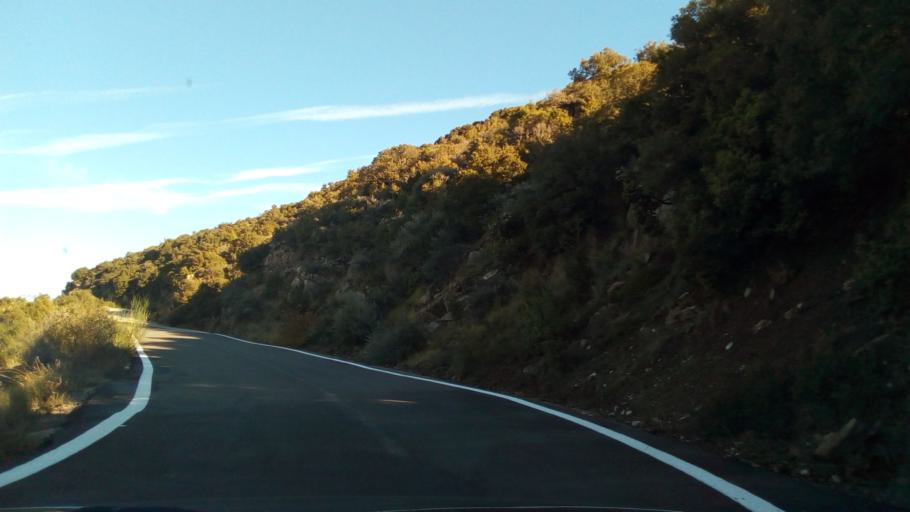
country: GR
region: West Greece
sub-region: Nomos Aitolias kai Akarnanias
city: Nafpaktos
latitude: 38.5060
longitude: 21.8374
